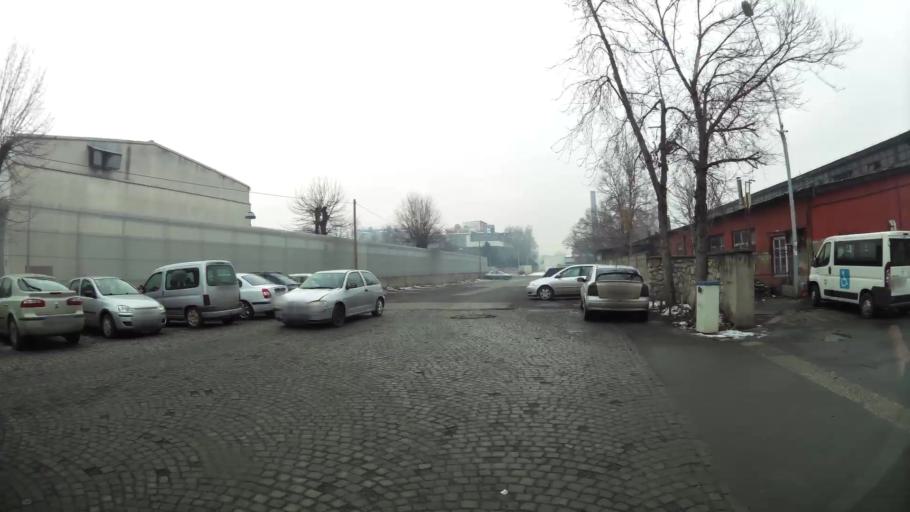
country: MK
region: Cair
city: Cair
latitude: 42.0003
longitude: 21.4652
